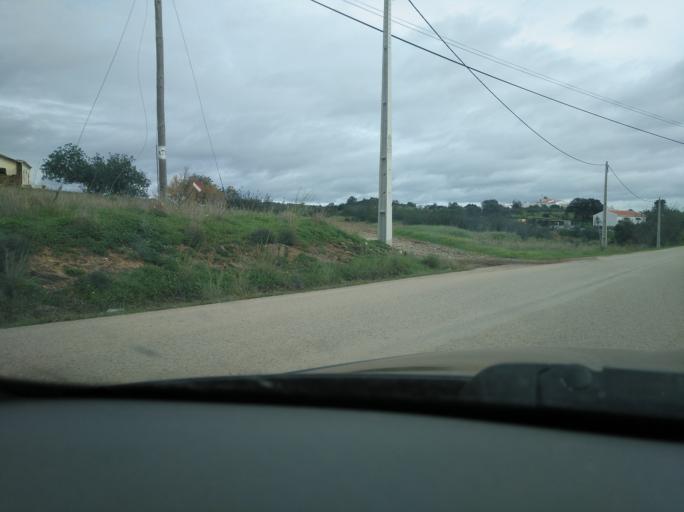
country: PT
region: Faro
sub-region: Castro Marim
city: Castro Marim
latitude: 37.2266
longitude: -7.4915
